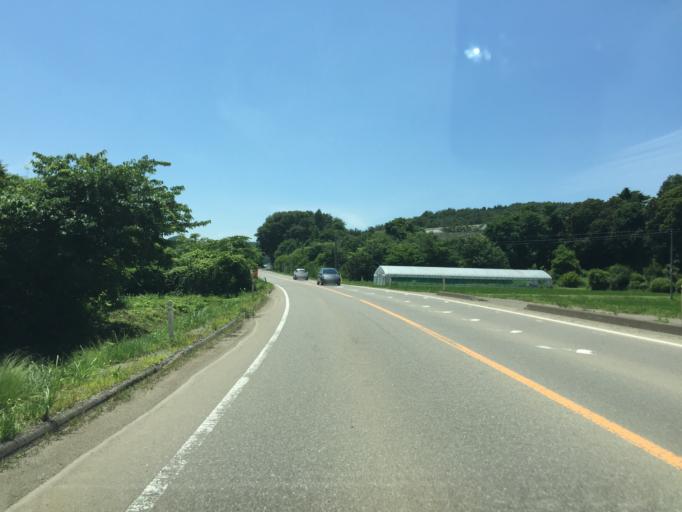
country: JP
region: Miyagi
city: Marumori
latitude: 37.7750
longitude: 140.7486
